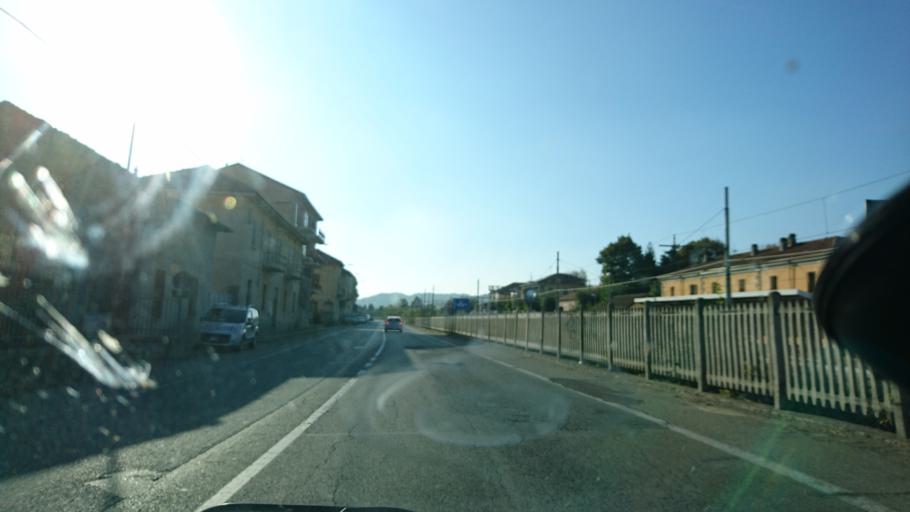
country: IT
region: Piedmont
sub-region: Provincia di Alessandria
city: Bistagno
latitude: 44.6591
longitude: 8.3728
